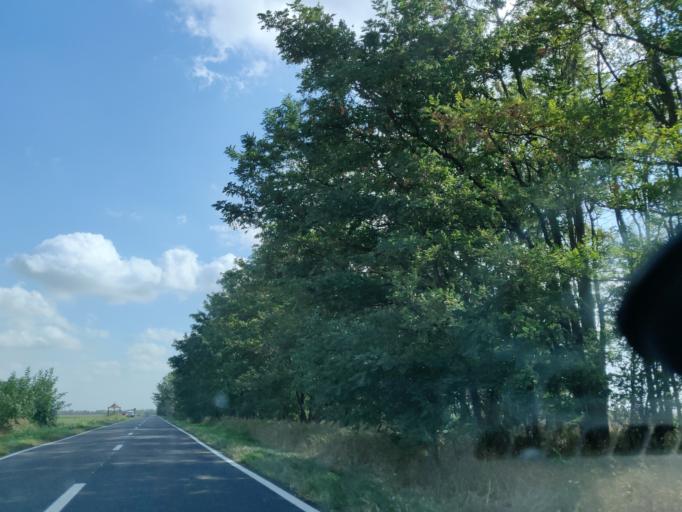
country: RO
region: Vrancea
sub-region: Comuna Ciorasti
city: Mihalceni
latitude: 45.4516
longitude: 27.3834
